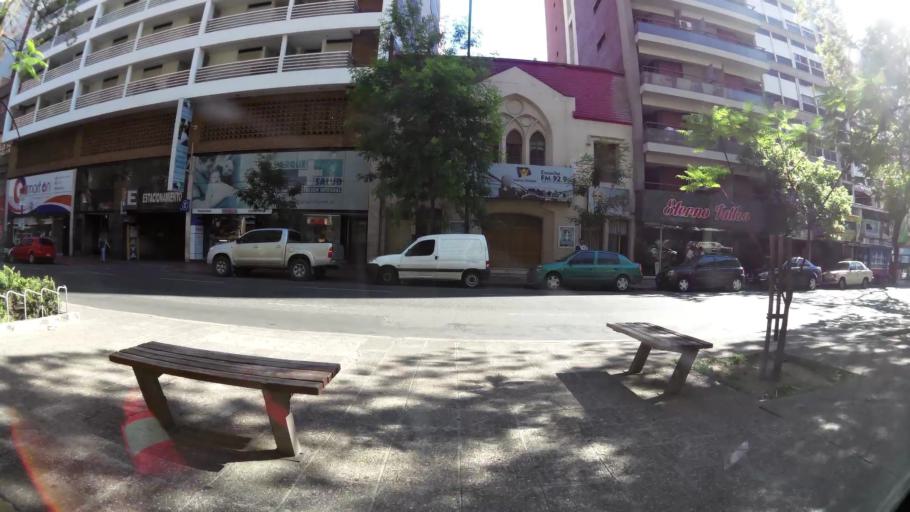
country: AR
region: Cordoba
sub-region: Departamento de Capital
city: Cordoba
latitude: -31.4217
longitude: -64.1825
